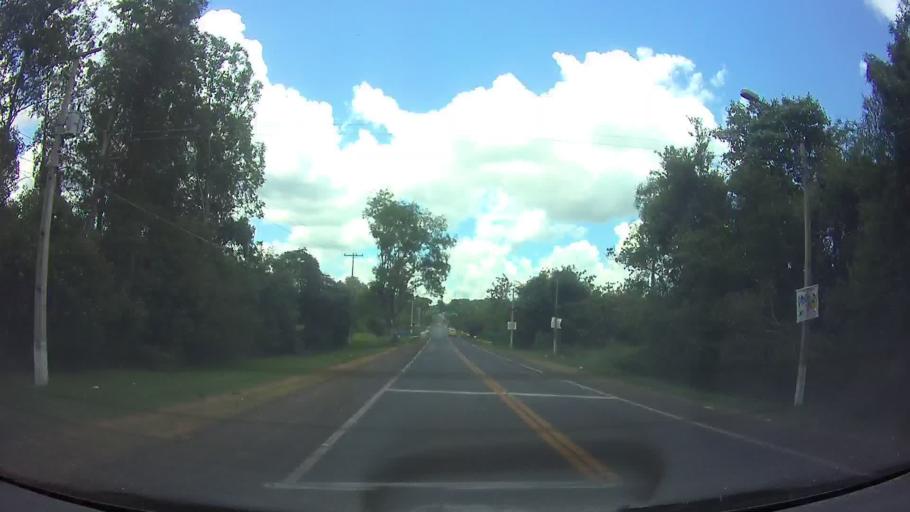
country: PY
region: Central
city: Capiata
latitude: -25.3484
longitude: -57.4169
